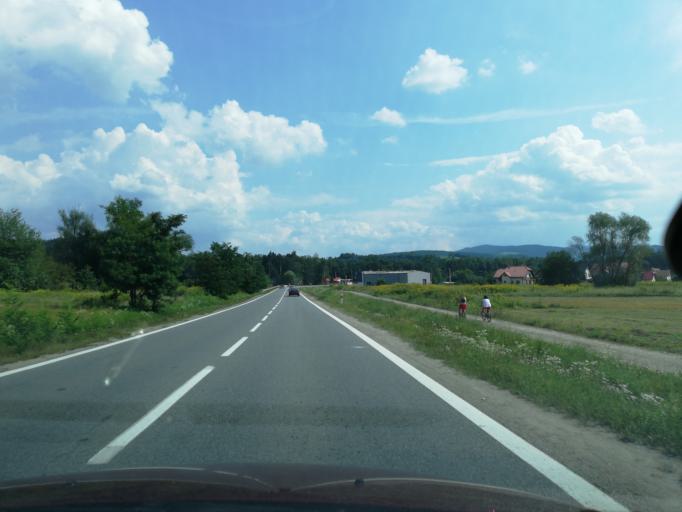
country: PL
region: Lesser Poland Voivodeship
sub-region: Powiat nowosadecki
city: Stary Sacz
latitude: 49.5708
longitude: 20.6523
